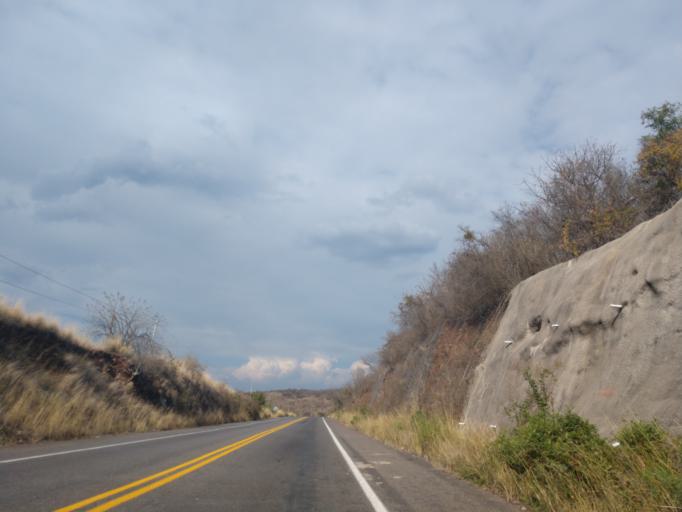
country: MX
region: Jalisco
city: La Manzanilla de la Paz
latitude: 20.0792
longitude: -103.1692
